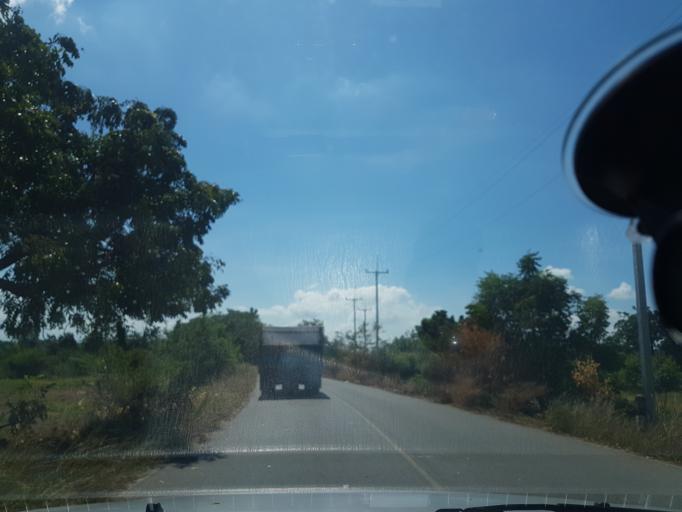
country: TH
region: Lop Buri
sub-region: Amphoe Tha Luang
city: Tha Luang
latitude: 14.9904
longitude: 101.0110
